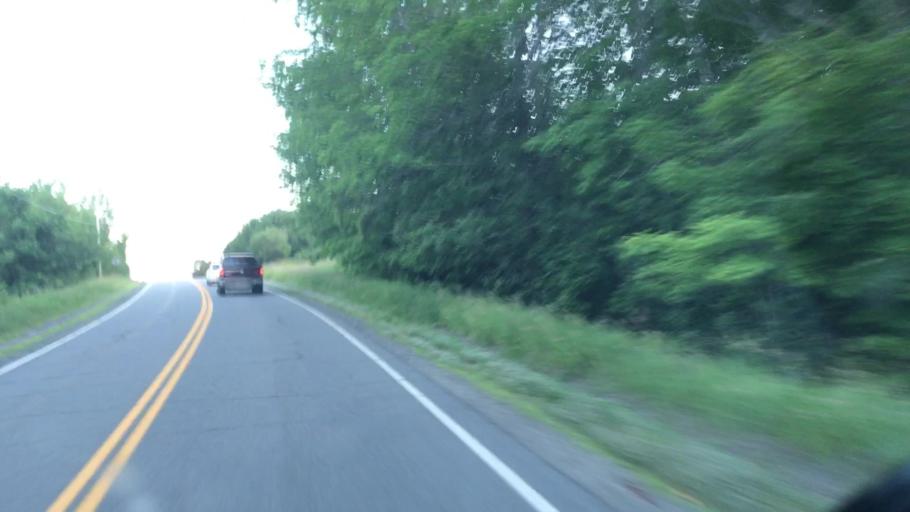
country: US
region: Maine
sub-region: Penobscot County
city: Medway
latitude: 45.6165
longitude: -68.3030
